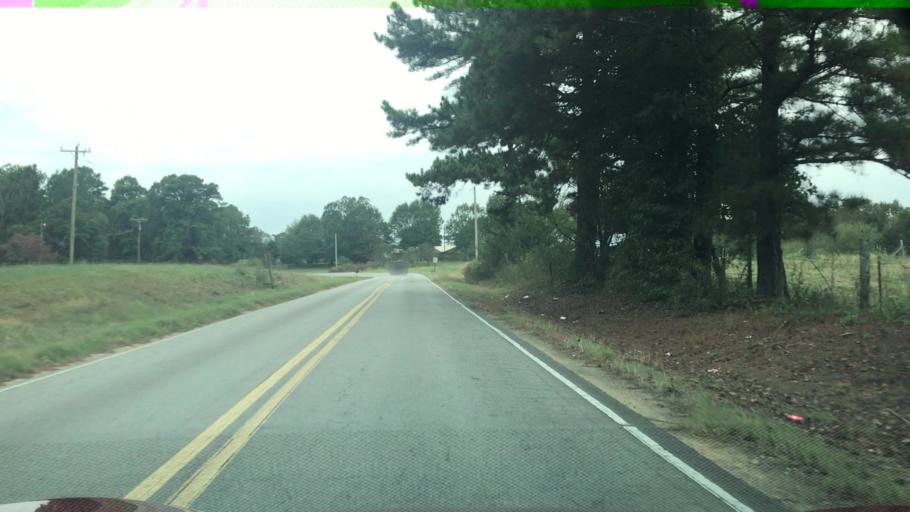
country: US
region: Alabama
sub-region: Cullman County
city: Good Hope
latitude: 34.0961
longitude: -87.0475
